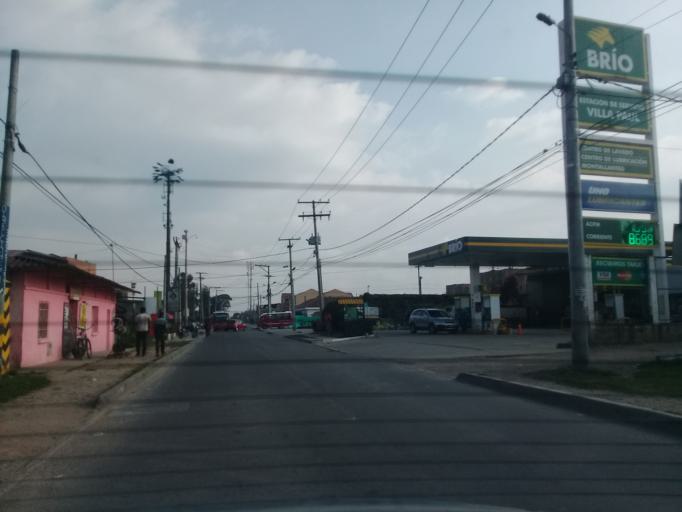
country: CO
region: Cundinamarca
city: Funza
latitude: 4.7313
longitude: -74.2202
